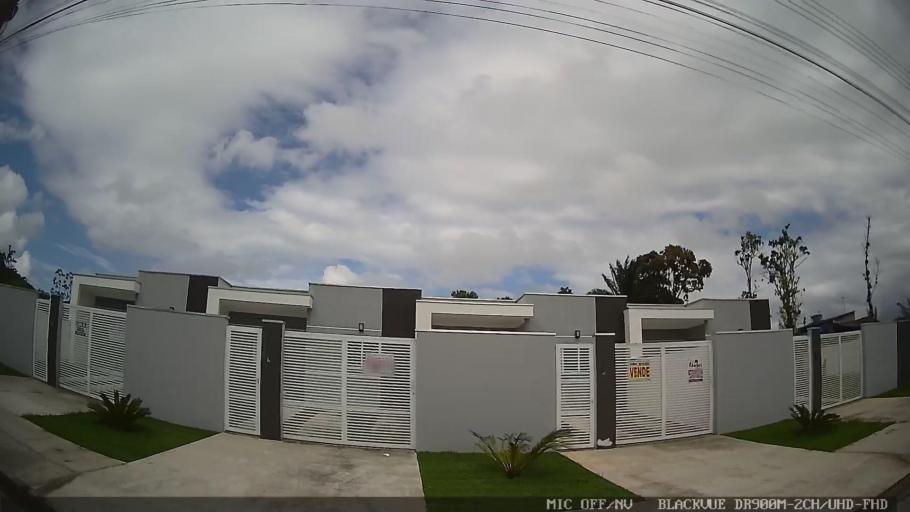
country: BR
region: Sao Paulo
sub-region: Caraguatatuba
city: Caraguatatuba
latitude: -23.6402
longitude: -45.4445
